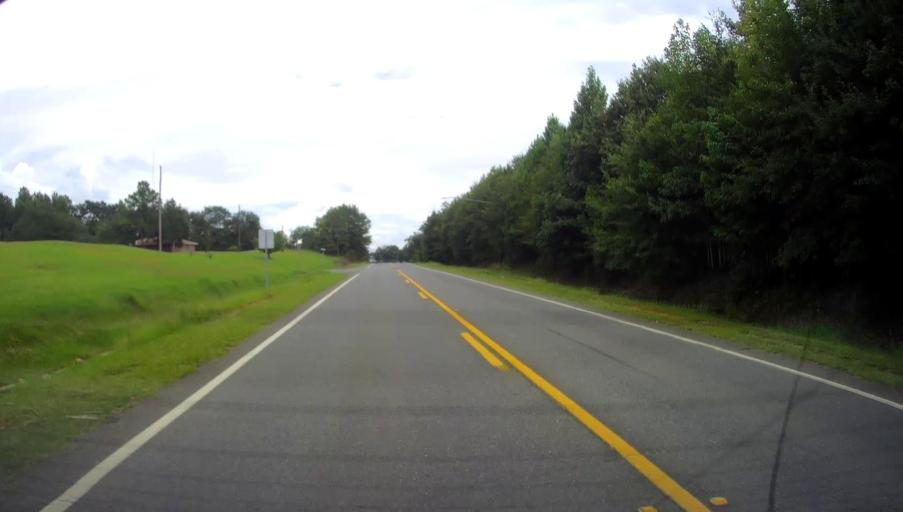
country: US
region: Georgia
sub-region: Marion County
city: Buena Vista
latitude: 32.3181
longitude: -84.5267
